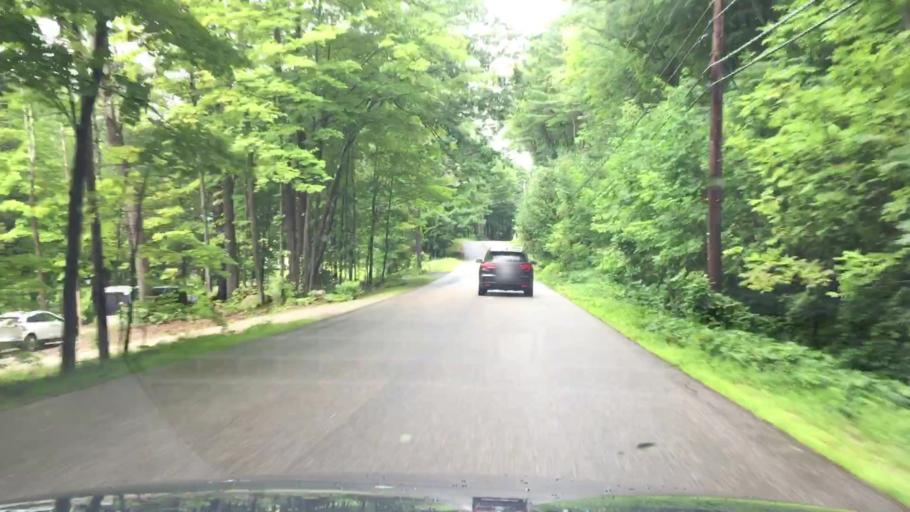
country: US
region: New Hampshire
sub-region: Grafton County
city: Holderness
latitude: 43.7258
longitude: -71.5716
